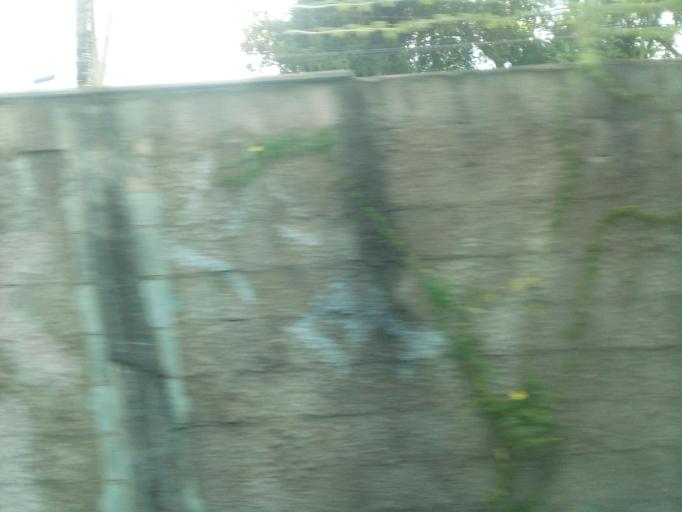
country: BR
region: Minas Gerais
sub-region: Belo Horizonte
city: Belo Horizonte
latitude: -19.8801
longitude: -43.8598
